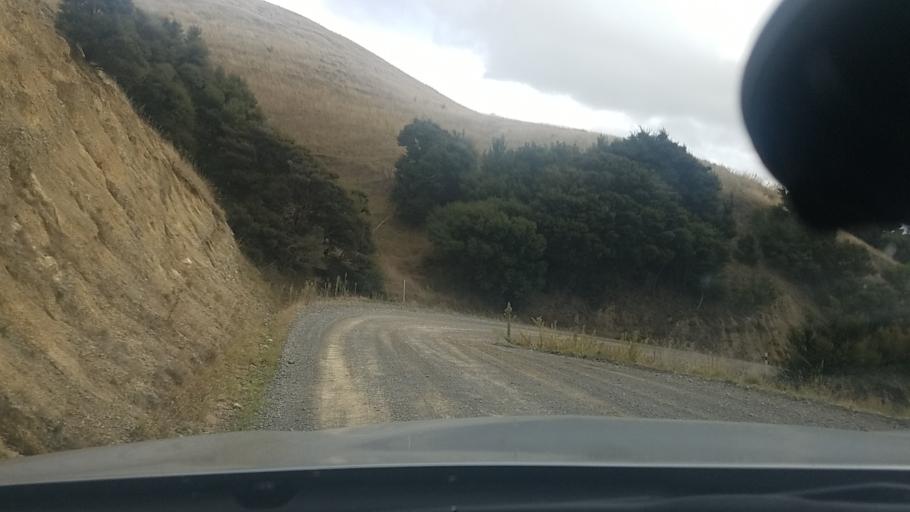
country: NZ
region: Marlborough
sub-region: Marlborough District
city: Blenheim
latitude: -41.5860
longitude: 174.0735
